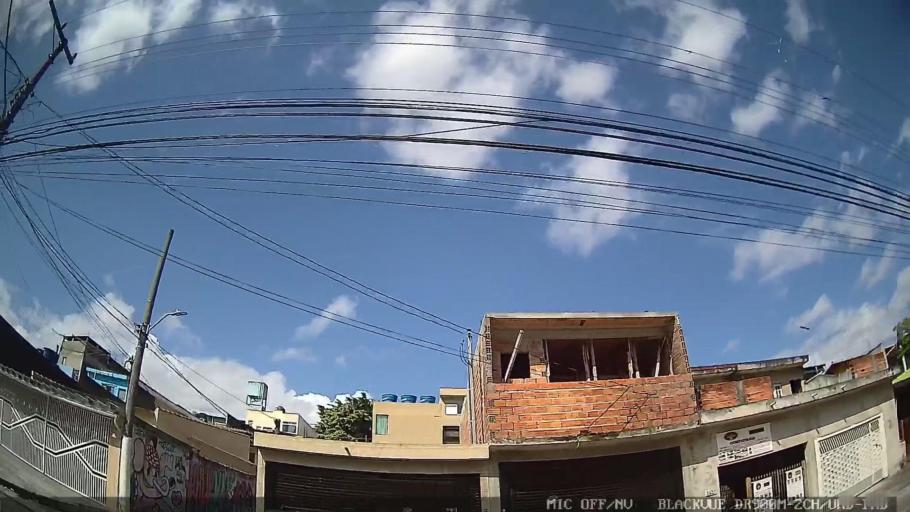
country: BR
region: Sao Paulo
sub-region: Guarulhos
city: Guarulhos
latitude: -23.5043
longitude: -46.4667
